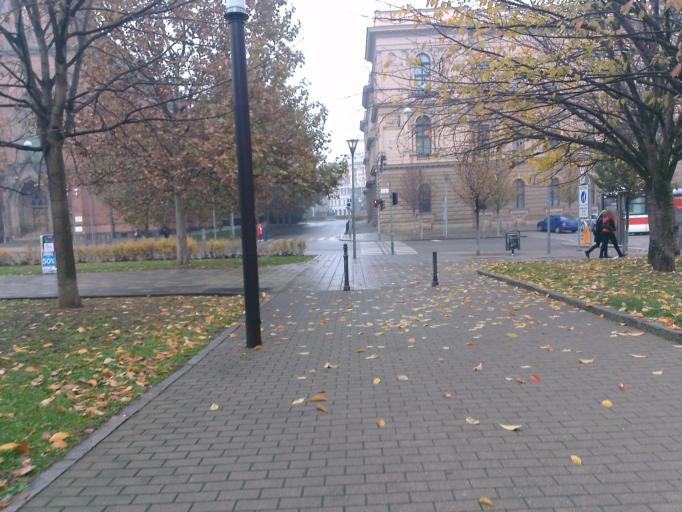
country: CZ
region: South Moravian
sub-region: Mesto Brno
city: Brno
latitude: 49.1970
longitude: 16.6039
